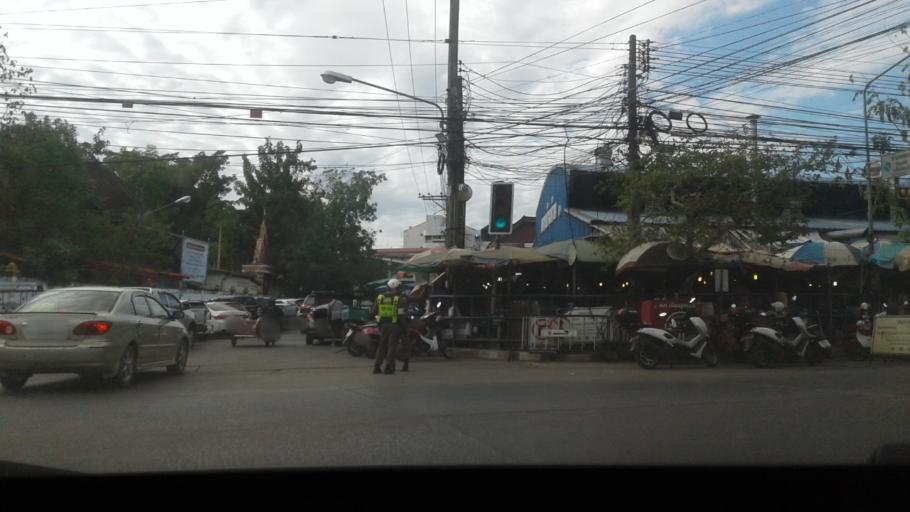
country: TH
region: Changwat Udon Thani
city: Udon Thani
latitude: 17.4164
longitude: 102.7915
